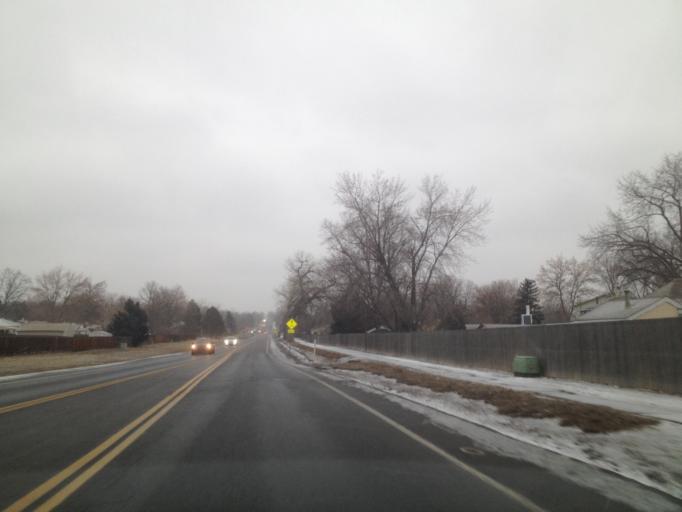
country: US
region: Colorado
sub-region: Jefferson County
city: Arvada
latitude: 39.8271
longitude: -105.1350
